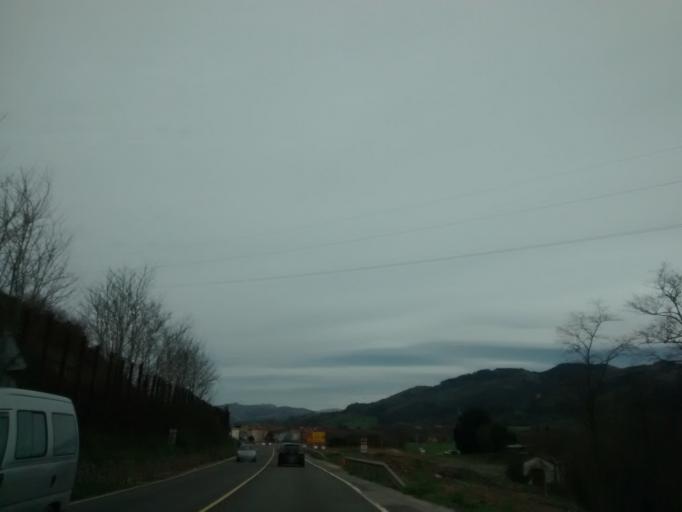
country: ES
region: Cantabria
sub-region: Provincia de Cantabria
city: Puente Viesgo
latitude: 43.3114
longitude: -3.9427
